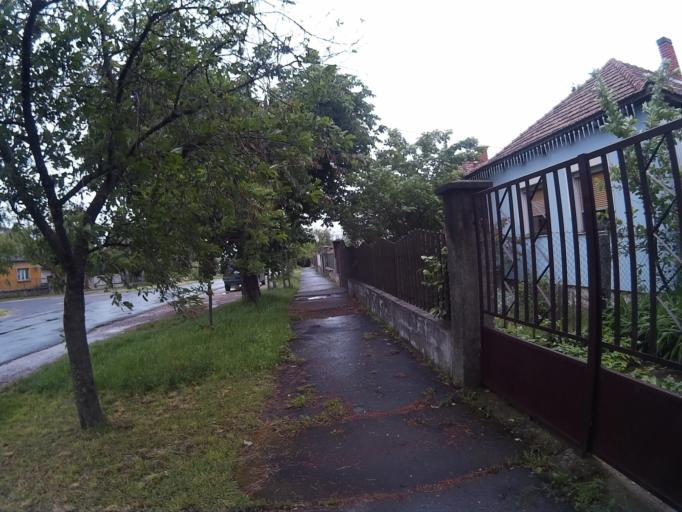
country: HU
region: Veszprem
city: Sumeg
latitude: 46.9725
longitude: 17.2853
